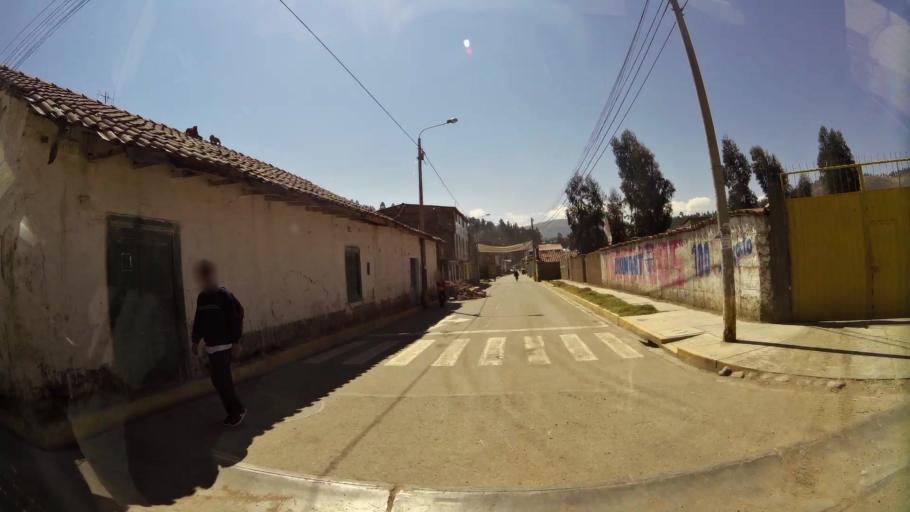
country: PE
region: Junin
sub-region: Provincia de Concepcion
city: Concepcion
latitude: -11.9177
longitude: -75.3165
